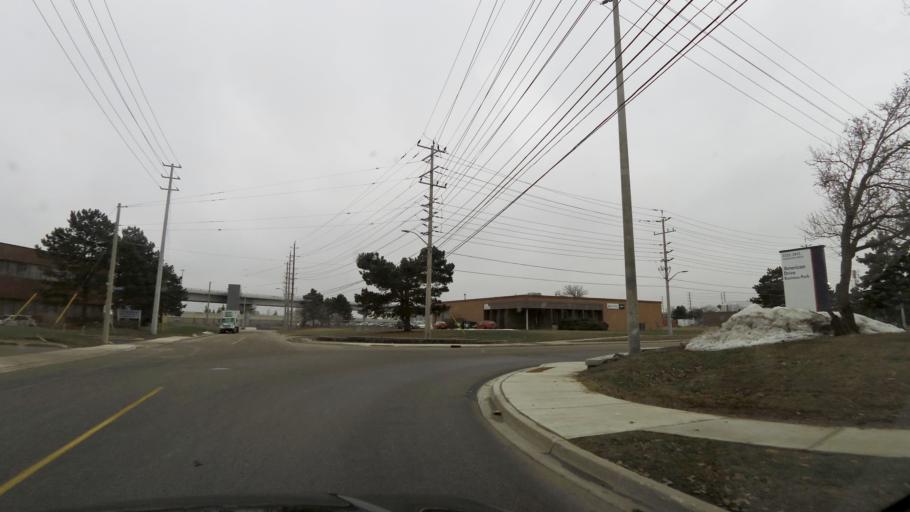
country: CA
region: Ontario
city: Etobicoke
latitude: 43.6986
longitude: -79.6116
